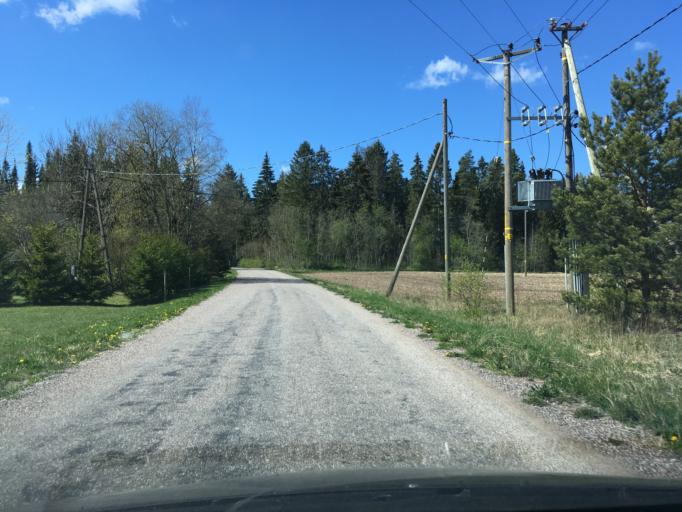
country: EE
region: Harju
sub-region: Rae vald
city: Vaida
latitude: 59.2004
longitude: 25.0821
